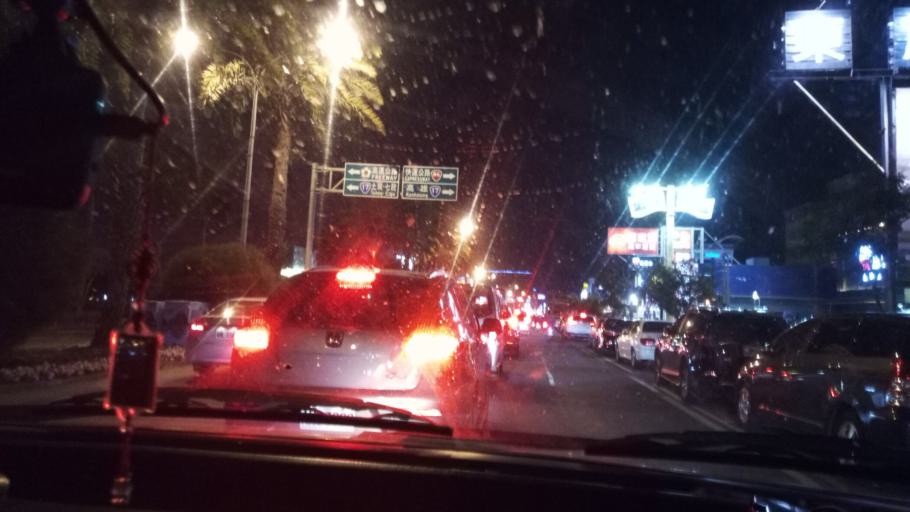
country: TW
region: Taiwan
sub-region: Tainan
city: Tainan
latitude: 22.9892
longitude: 120.1854
